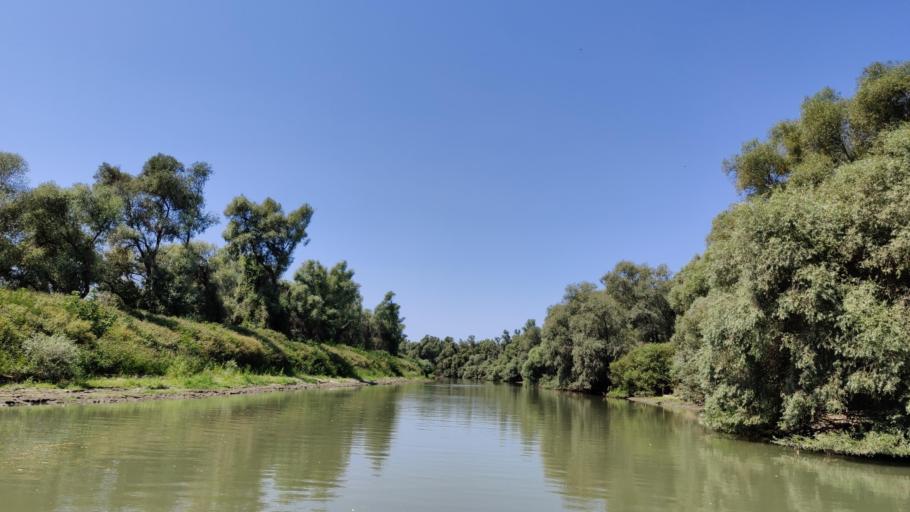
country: RO
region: Tulcea
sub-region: Comuna Pardina
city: Pardina
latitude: 45.2557
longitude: 28.9608
